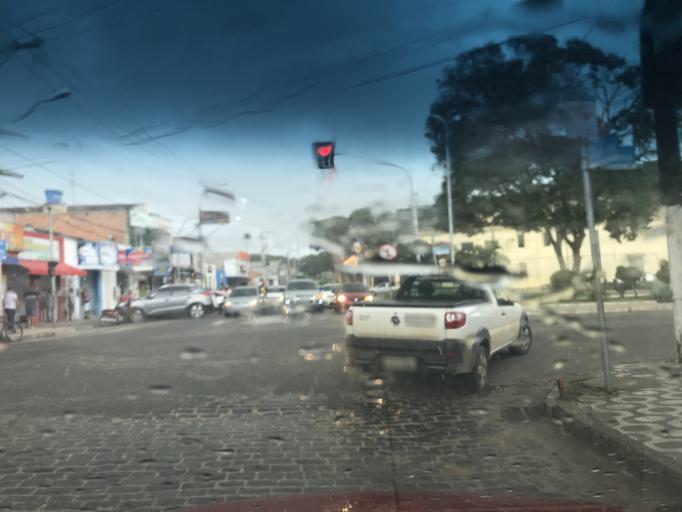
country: BR
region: Bahia
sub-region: Cruz Das Almas
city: Cruz das Almas
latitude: -12.6736
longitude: -39.1002
